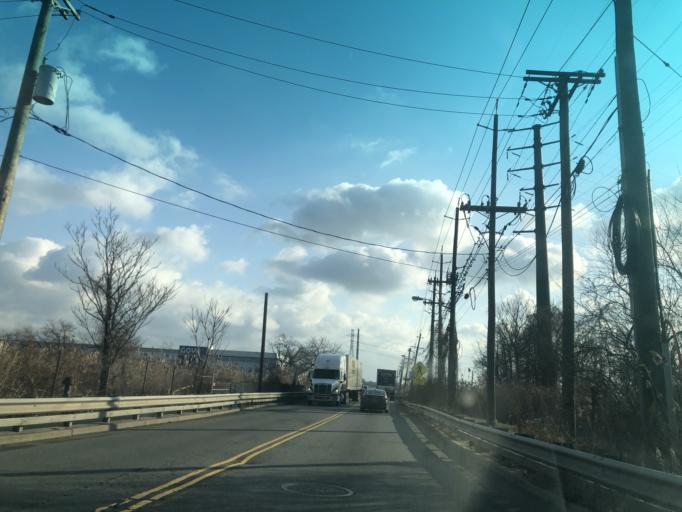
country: US
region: New Jersey
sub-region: Hudson County
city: Secaucus
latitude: 40.7630
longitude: -74.0685
